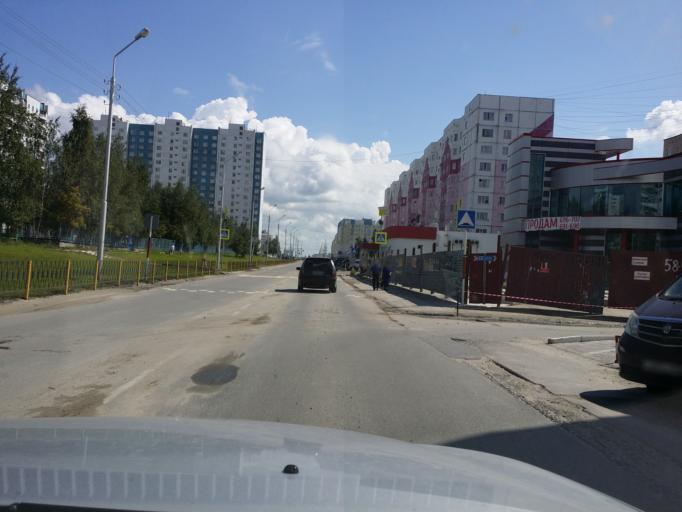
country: RU
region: Khanty-Mansiyskiy Avtonomnyy Okrug
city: Nizhnevartovsk
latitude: 60.9299
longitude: 76.6008
